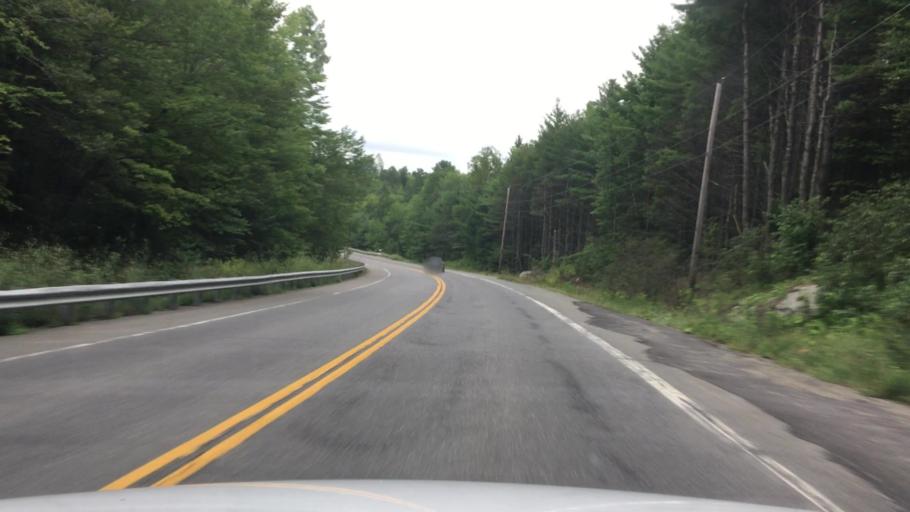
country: US
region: Maine
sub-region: Penobscot County
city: Bradley
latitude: 44.8248
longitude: -68.4092
